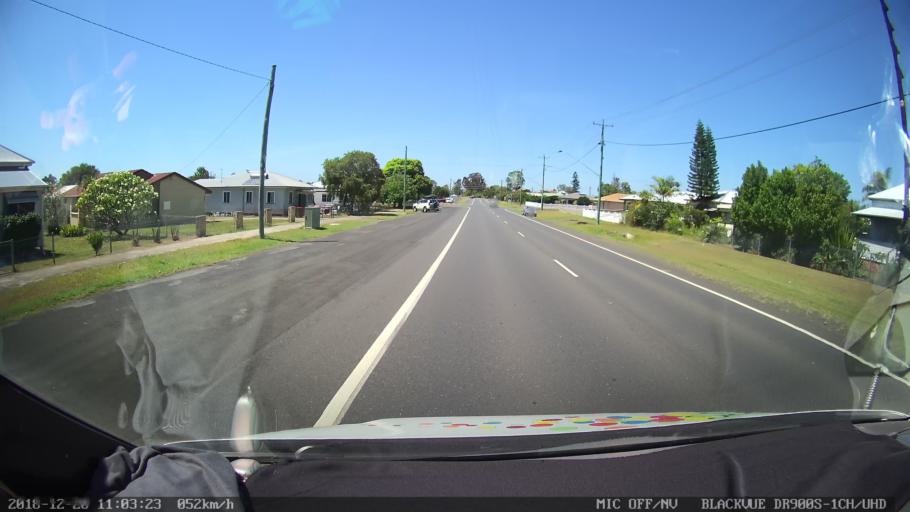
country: AU
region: New South Wales
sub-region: Richmond Valley
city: Casino
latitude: -28.8767
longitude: 153.0431
